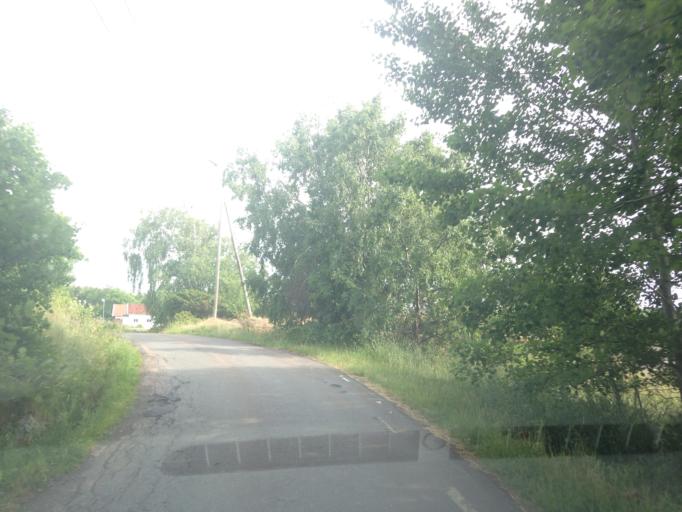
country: SE
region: Vaestra Goetaland
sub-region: Goteborg
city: Majorna
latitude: 57.7566
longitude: 11.8647
